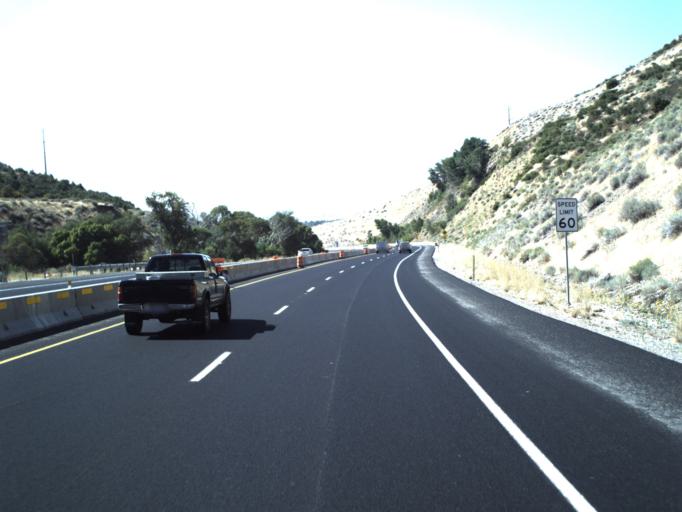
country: US
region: Utah
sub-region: Box Elder County
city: Brigham City
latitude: 41.4983
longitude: -111.9787
